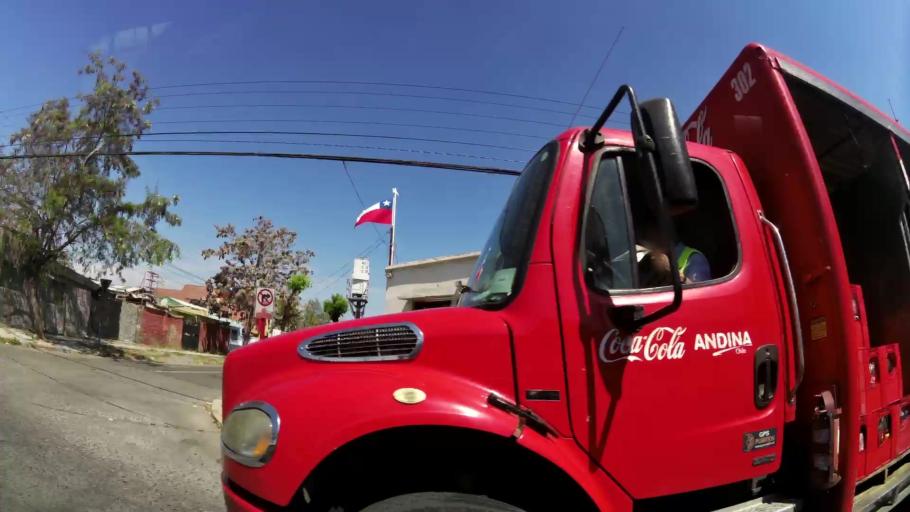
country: CL
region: Santiago Metropolitan
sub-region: Provincia de Santiago
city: La Pintana
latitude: -33.5313
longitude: -70.6442
